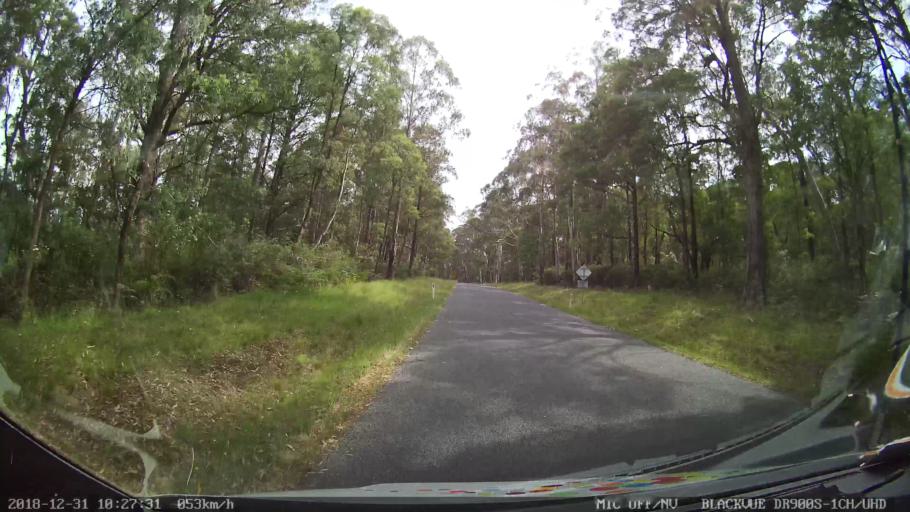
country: AU
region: New South Wales
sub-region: Snowy River
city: Jindabyne
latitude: -36.4862
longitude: 148.1446
